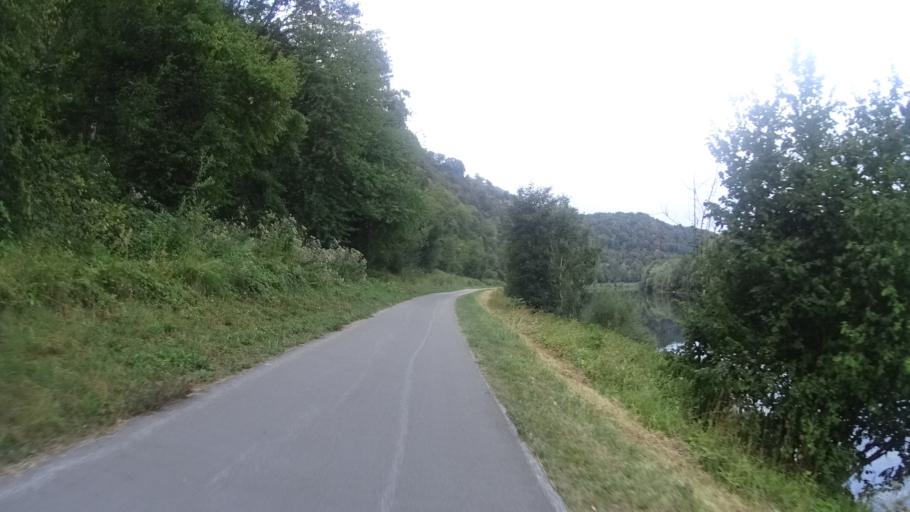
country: FR
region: Franche-Comte
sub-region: Departement du Doubs
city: Morre
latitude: 47.2280
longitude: 6.0544
